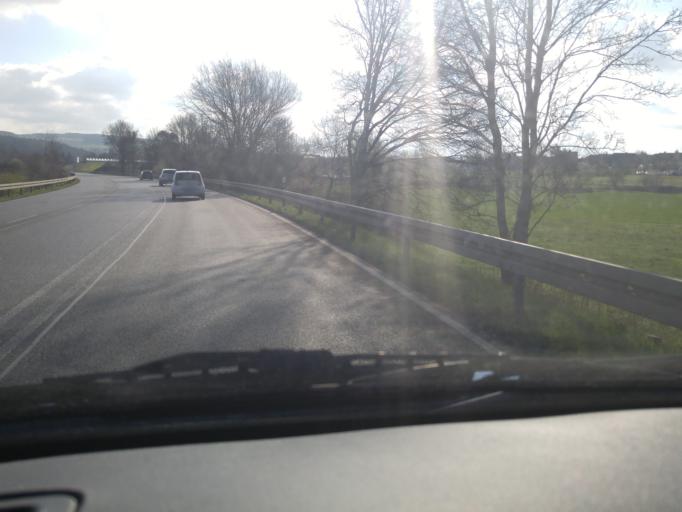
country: DE
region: Hesse
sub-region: Regierungsbezirk Kassel
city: Grossenluder
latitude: 50.5756
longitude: 9.5562
